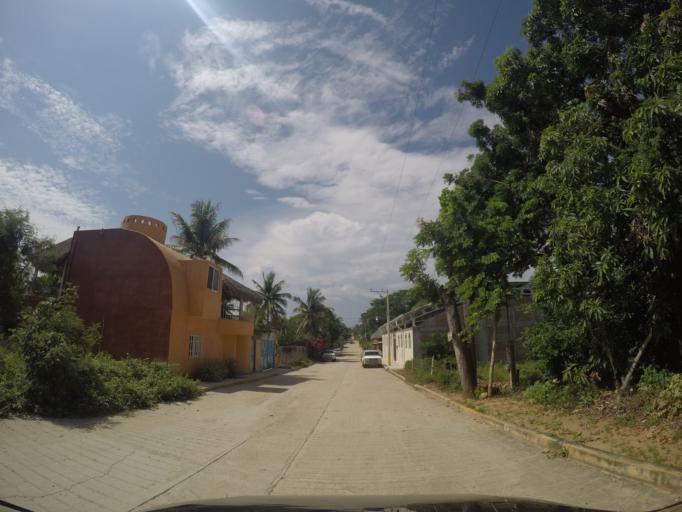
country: MX
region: Oaxaca
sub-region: Santa Maria Colotepec
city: Brisas de Zicatela
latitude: 15.8325
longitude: -97.0426
